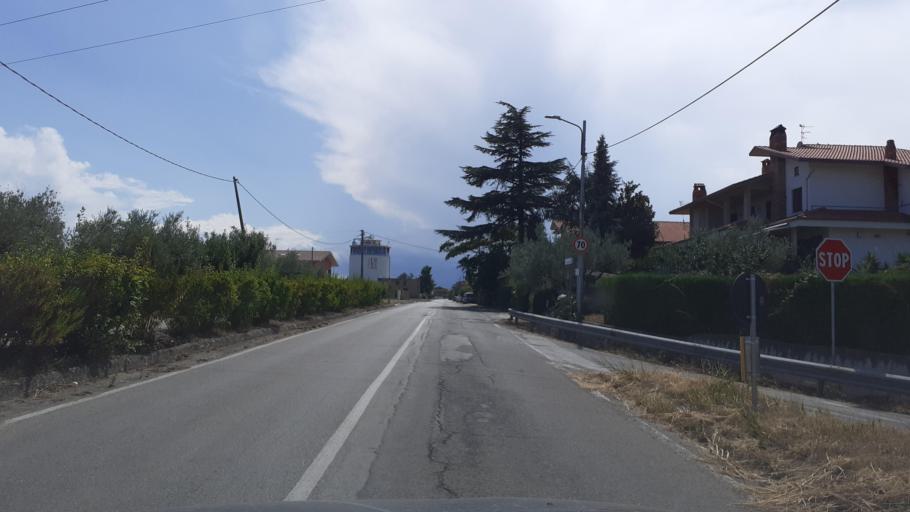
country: IT
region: Abruzzo
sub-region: Provincia di Chieti
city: Rocca San Giovanni
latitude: 42.2450
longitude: 14.4594
